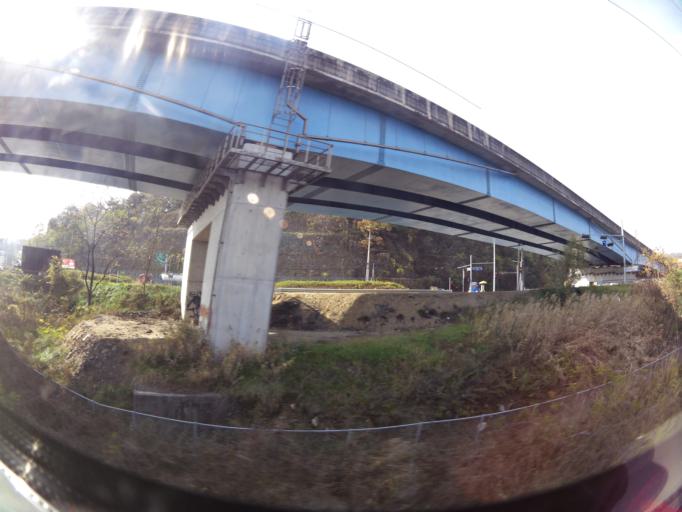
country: KR
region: Chungcheongbuk-do
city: Cheongju-si
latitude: 36.6165
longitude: 127.2929
